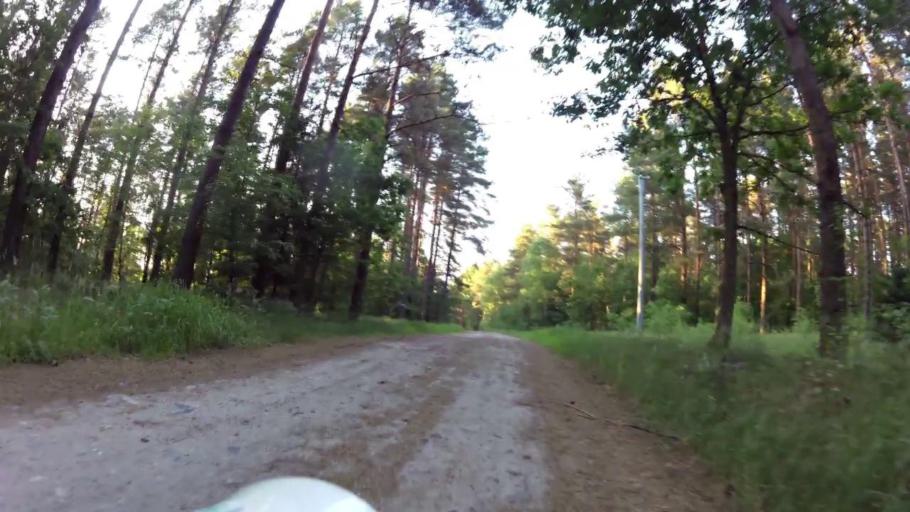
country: PL
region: West Pomeranian Voivodeship
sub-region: Powiat szczecinecki
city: Szczecinek
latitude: 53.8307
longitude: 16.6880
